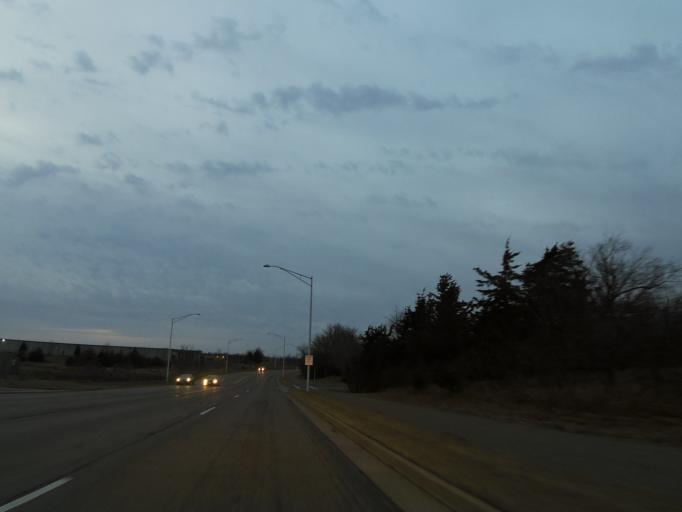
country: US
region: Wisconsin
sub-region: Saint Croix County
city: Hudson
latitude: 44.9491
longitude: -92.7054
